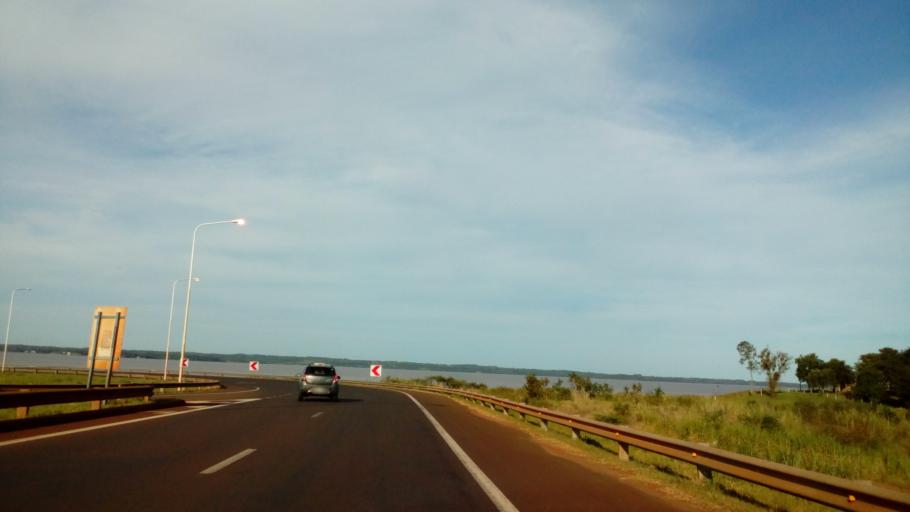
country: AR
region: Misiones
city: Garupa
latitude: -27.4449
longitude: -55.8481
